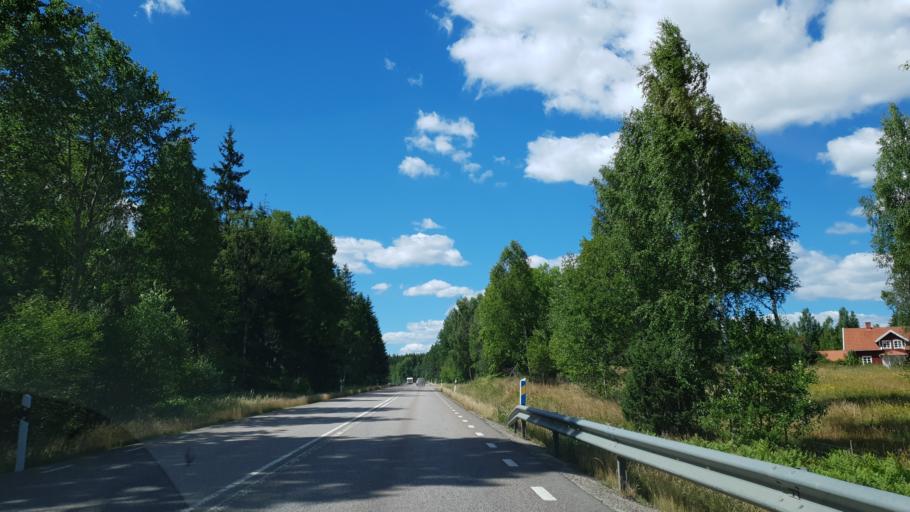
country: SE
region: Kronoberg
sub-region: Lessebo Kommun
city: Lessebo
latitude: 56.7768
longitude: 15.2522
